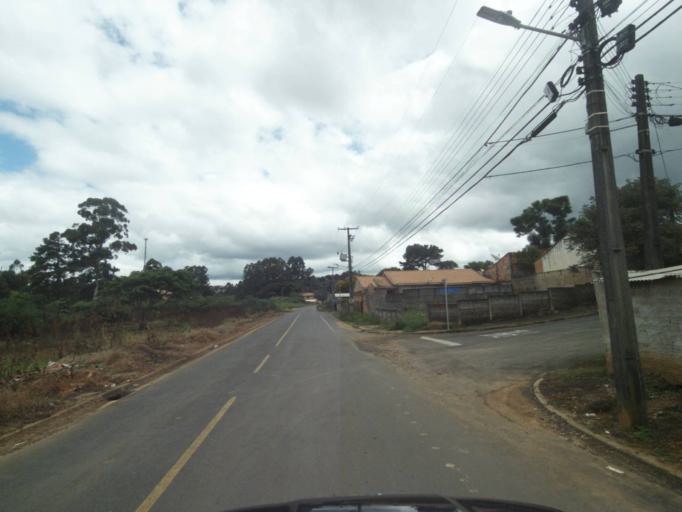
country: BR
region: Parana
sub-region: Telemaco Borba
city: Telemaco Borba
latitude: -24.3154
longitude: -50.6450
